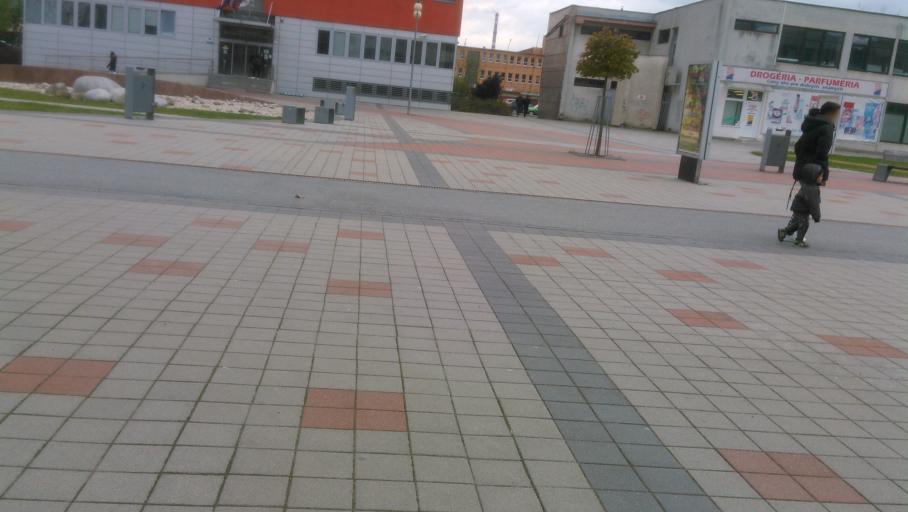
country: SK
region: Presovsky
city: Humenne
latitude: 48.9306
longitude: 21.9132
